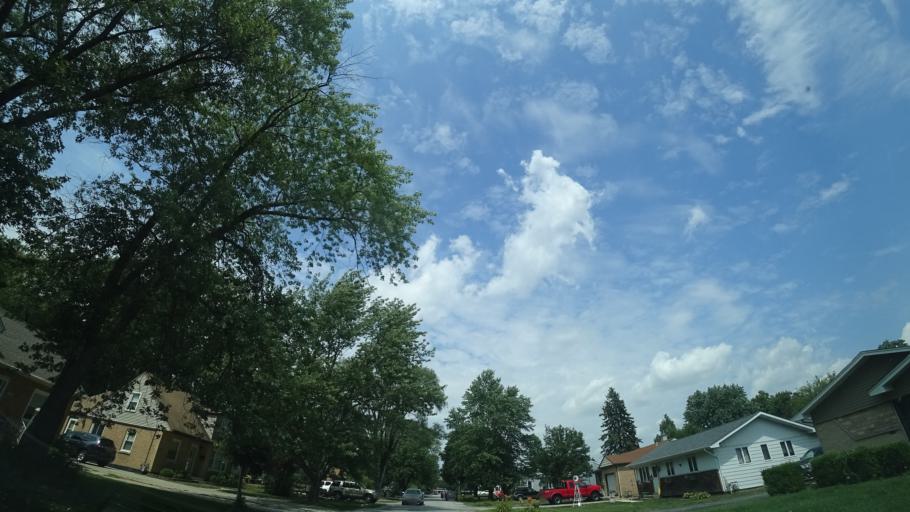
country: US
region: Illinois
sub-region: Cook County
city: Worth
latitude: 41.6868
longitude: -87.7859
